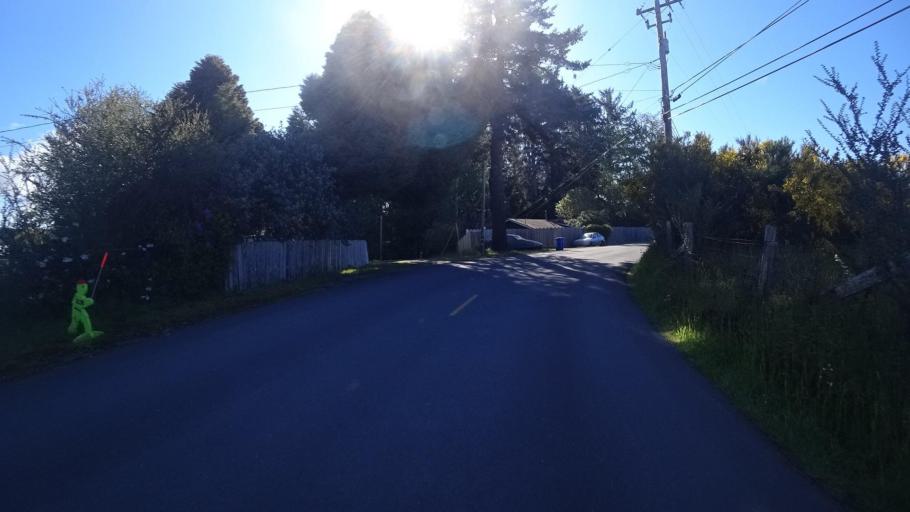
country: US
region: California
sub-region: Humboldt County
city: Westhaven-Moonstone
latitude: 41.0049
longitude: -124.1013
